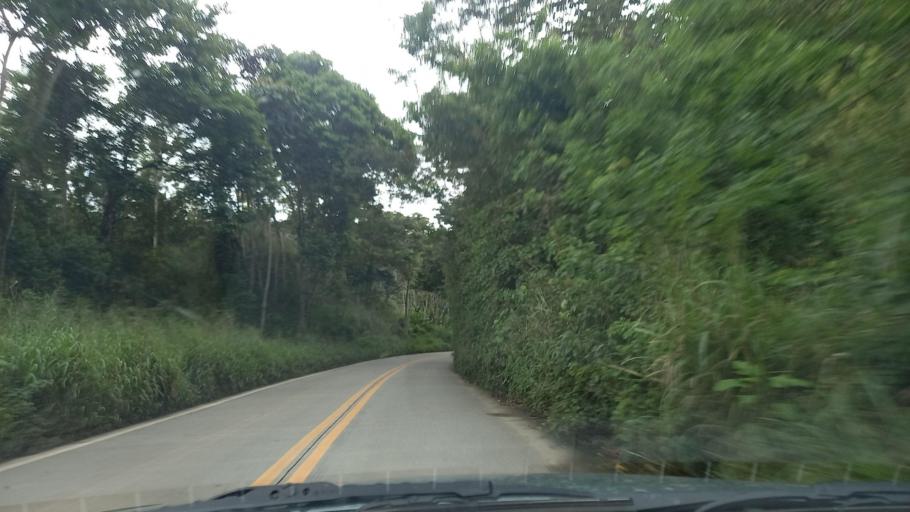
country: BR
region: Pernambuco
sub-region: Maraial
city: Maraial
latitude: -8.7664
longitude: -35.8622
